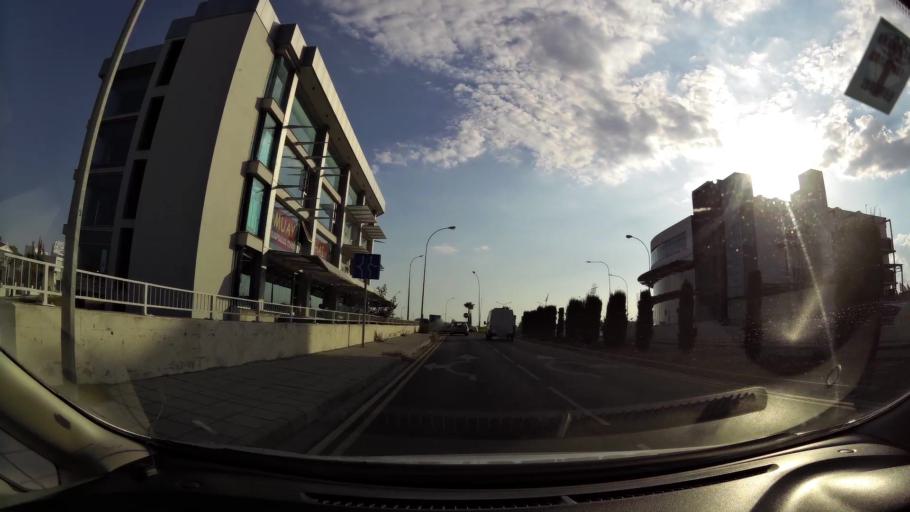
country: CY
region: Larnaka
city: Larnaca
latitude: 34.9291
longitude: 33.6045
